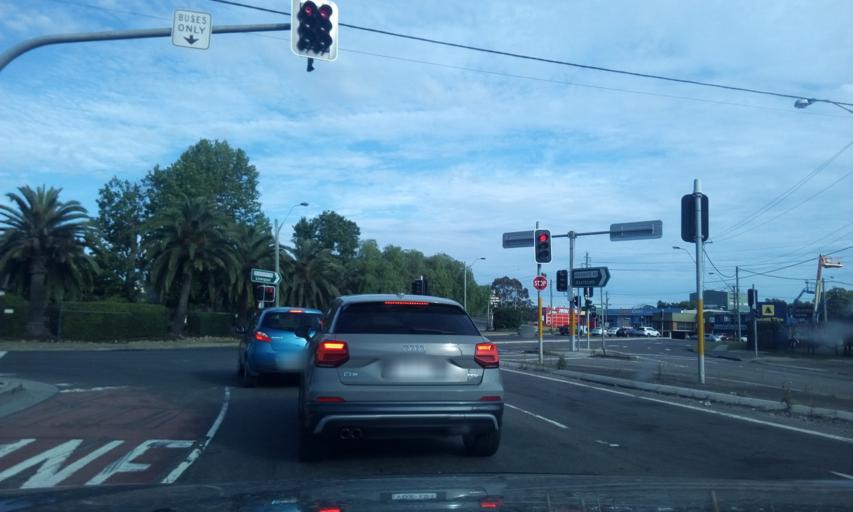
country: AU
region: New South Wales
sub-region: Fairfield
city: Liverpool
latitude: -33.9293
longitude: 150.9315
